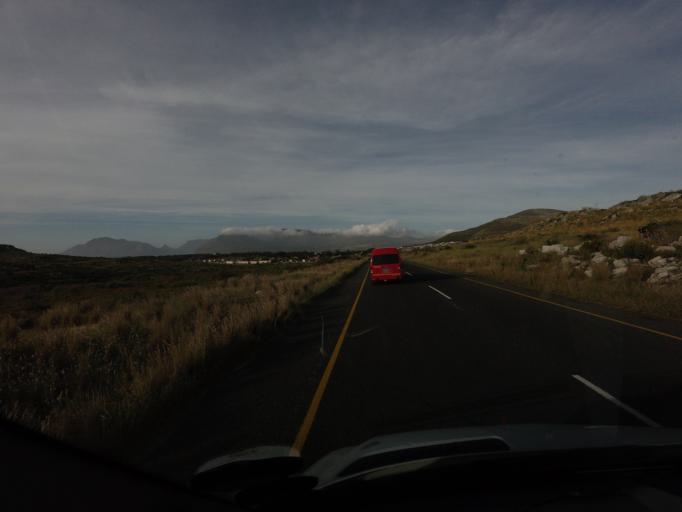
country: ZA
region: Western Cape
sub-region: City of Cape Town
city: Constantia
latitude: -34.1545
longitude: 18.3458
